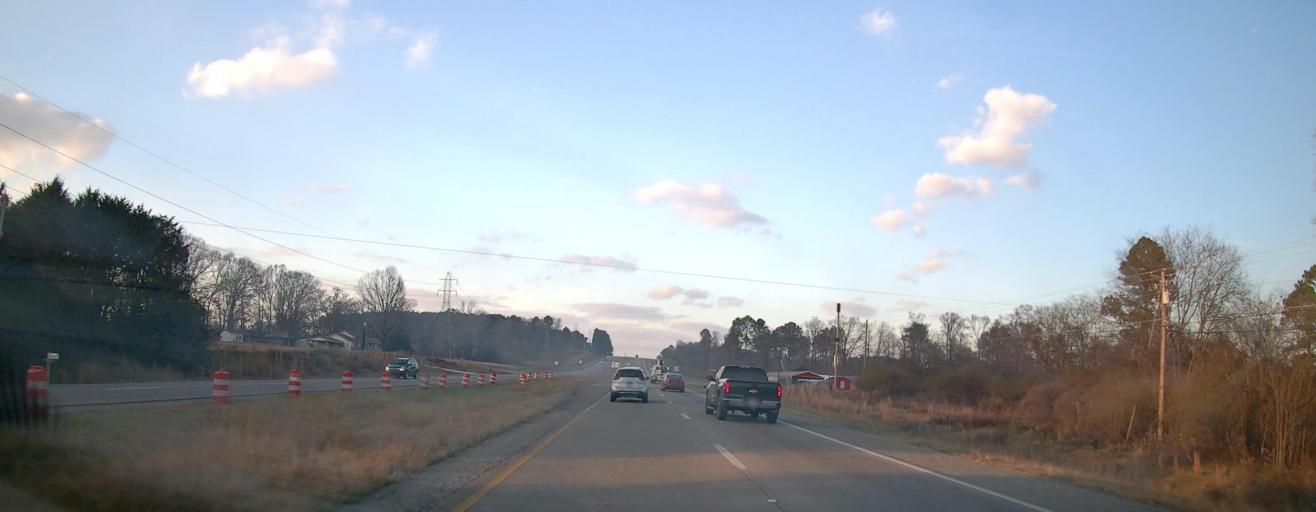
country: US
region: Alabama
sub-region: Calhoun County
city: Alexandria
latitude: 33.7870
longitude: -85.8975
